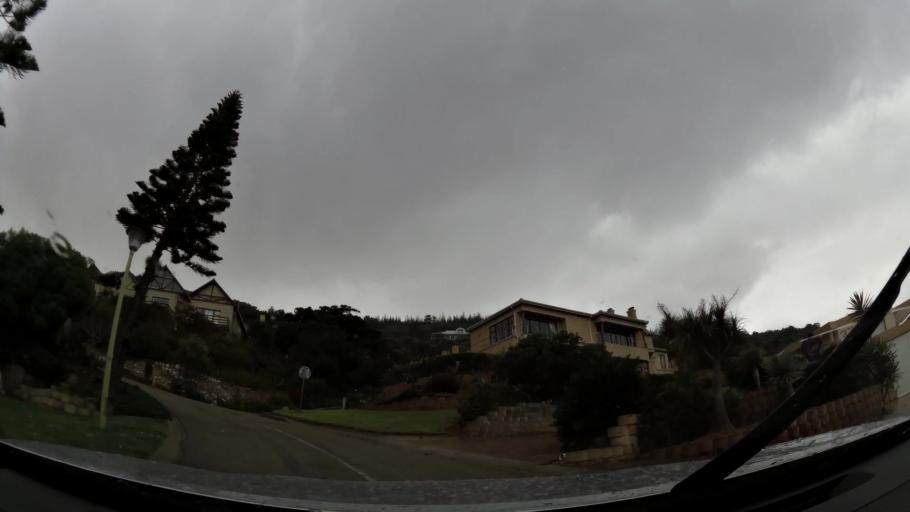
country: ZA
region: Western Cape
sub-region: Eden District Municipality
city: George
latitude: -34.0471
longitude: 22.2884
